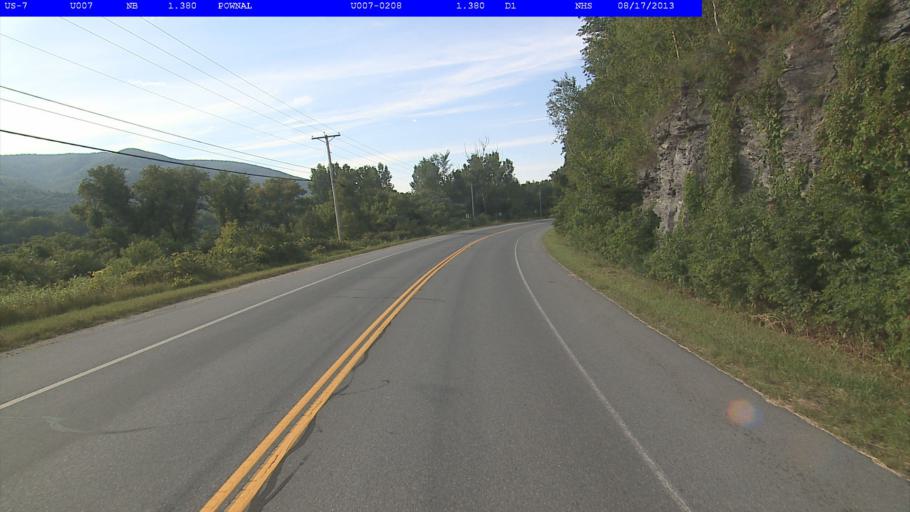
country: US
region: Massachusetts
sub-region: Berkshire County
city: Williamstown
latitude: 42.7566
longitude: -73.2311
